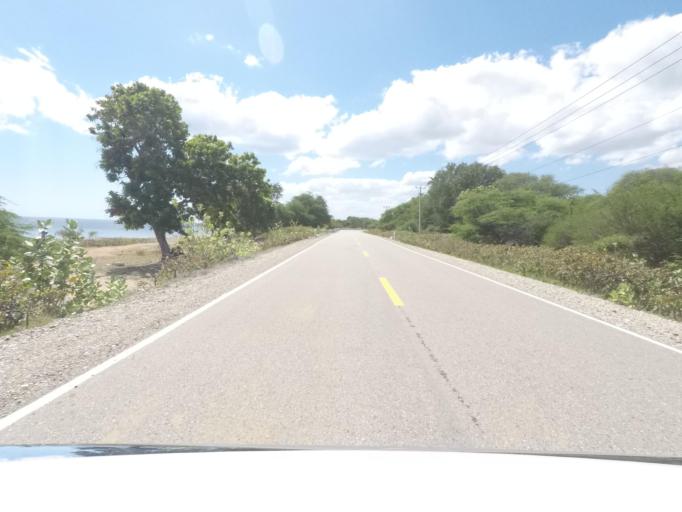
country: TL
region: Baucau
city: Baucau
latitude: -8.4268
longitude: 126.6932
